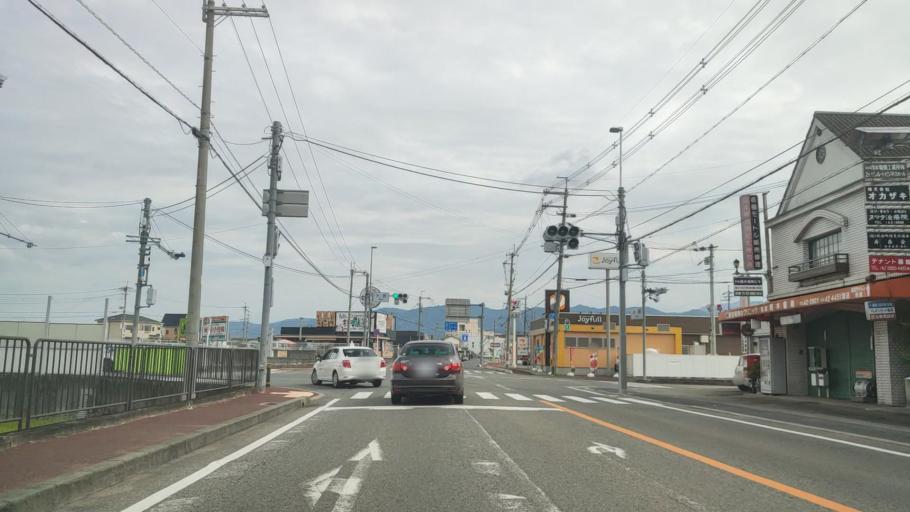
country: JP
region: Wakayama
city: Hashimoto
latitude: 34.3058
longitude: 135.5456
